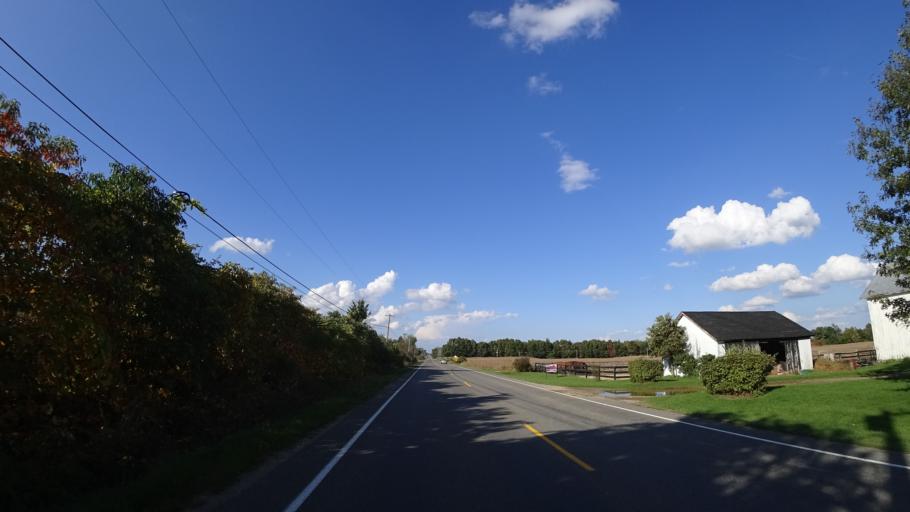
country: US
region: Michigan
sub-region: Saint Joseph County
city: Centreville
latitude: 41.8654
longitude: -85.5067
